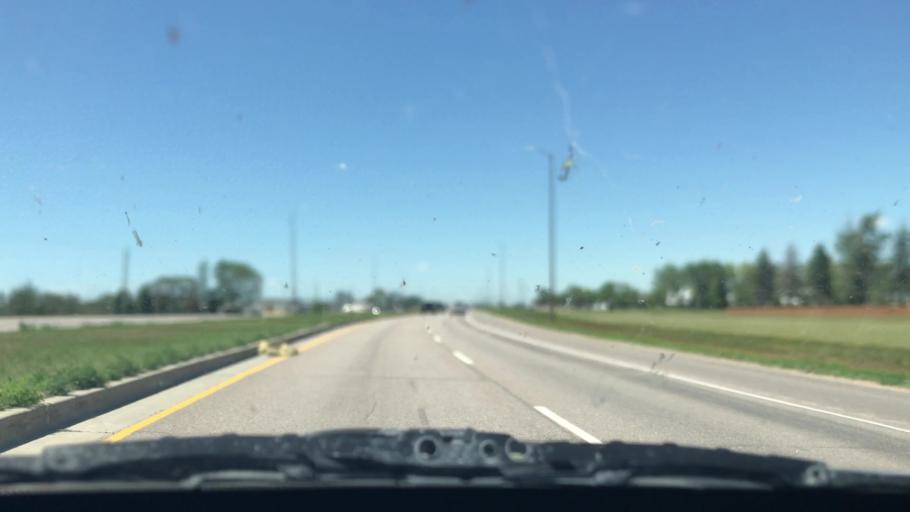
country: CA
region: Manitoba
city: Winnipeg
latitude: 49.8426
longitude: -96.9900
